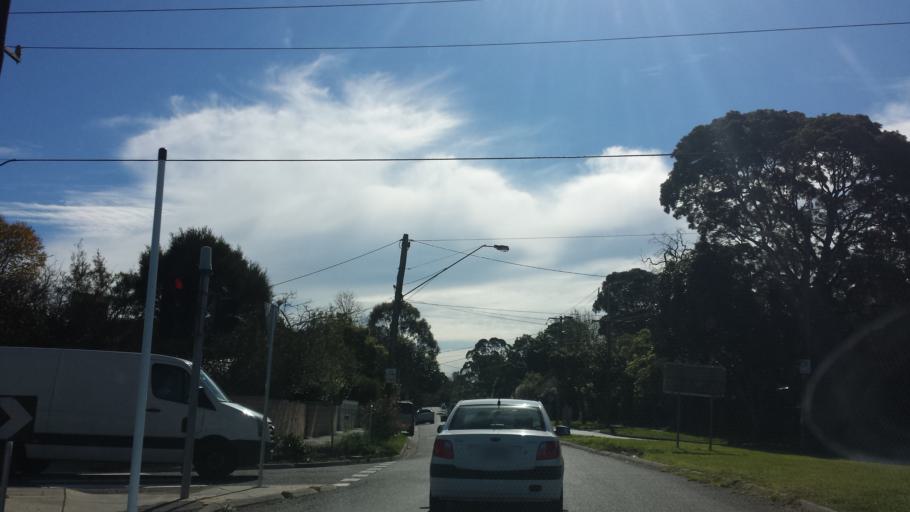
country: AU
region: Victoria
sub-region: Maroondah
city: Heathmont
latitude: -37.8252
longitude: 145.2517
